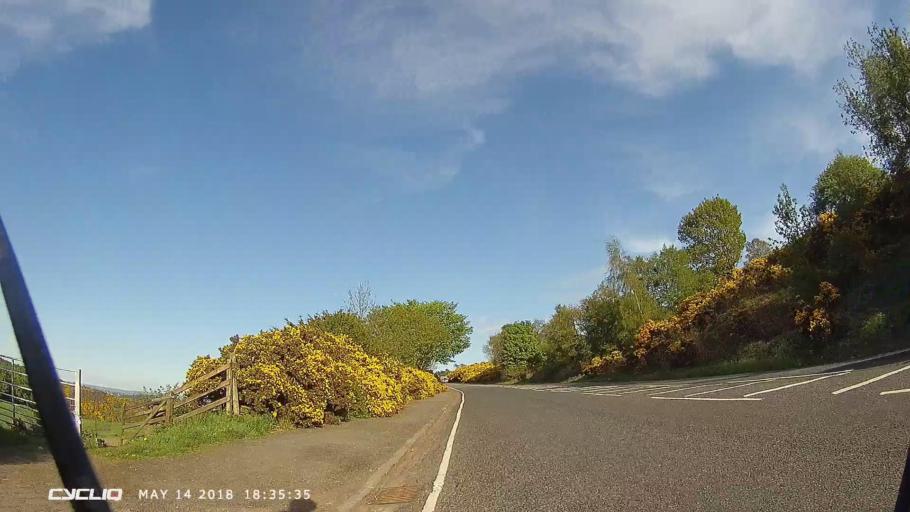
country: GB
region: Scotland
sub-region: Edinburgh
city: Edinburgh
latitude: 55.9180
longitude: -3.1981
